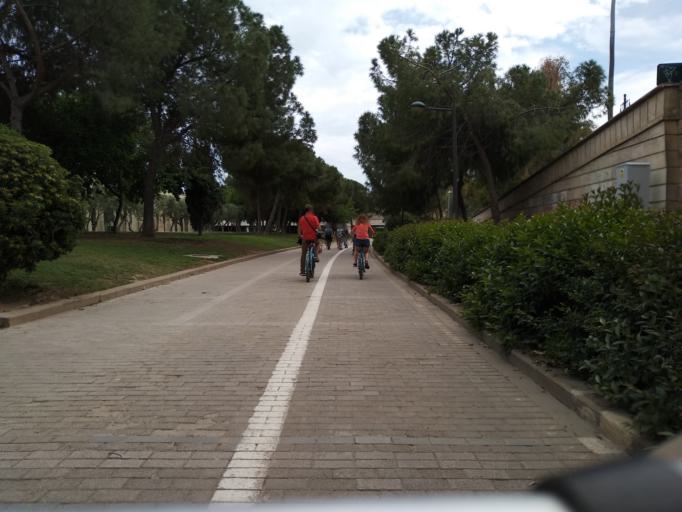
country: ES
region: Valencia
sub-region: Provincia de Valencia
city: Valencia
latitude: 39.4647
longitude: -0.3612
